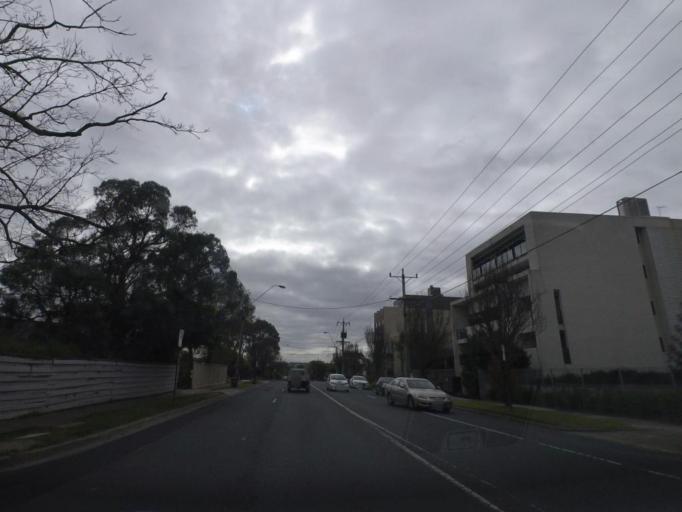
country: AU
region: Victoria
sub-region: Whitehorse
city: Box Hill
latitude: -37.8135
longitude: 145.1157
